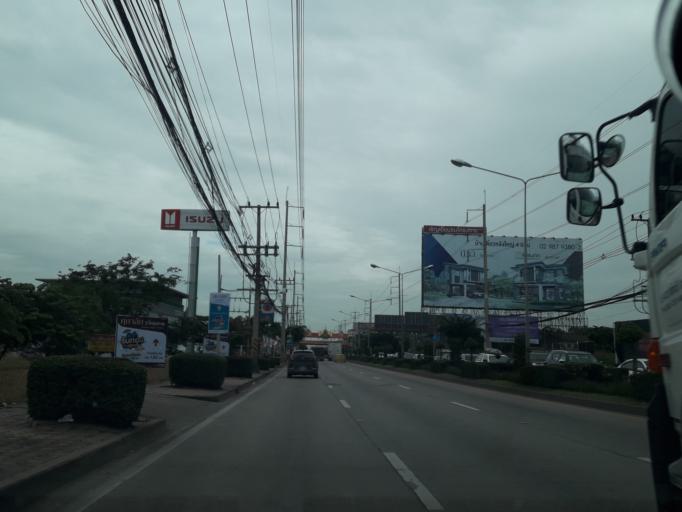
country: TH
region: Pathum Thani
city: Lam Luk Ka
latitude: 13.9347
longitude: 100.7429
